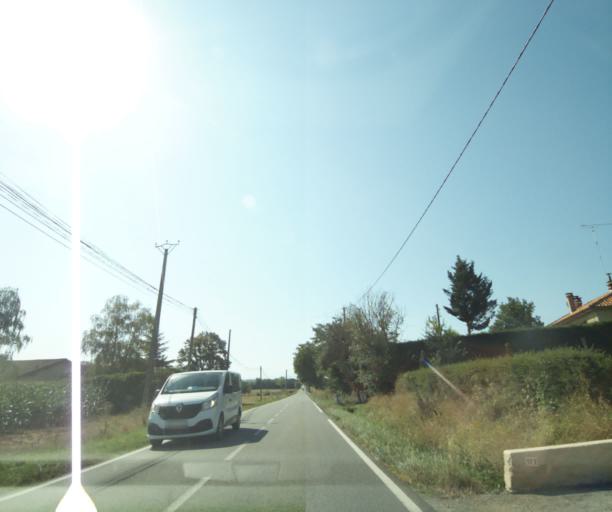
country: FR
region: Midi-Pyrenees
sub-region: Departement de la Haute-Garonne
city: Saint-Sulpice-sur-Leze
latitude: 43.3131
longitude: 1.3244
